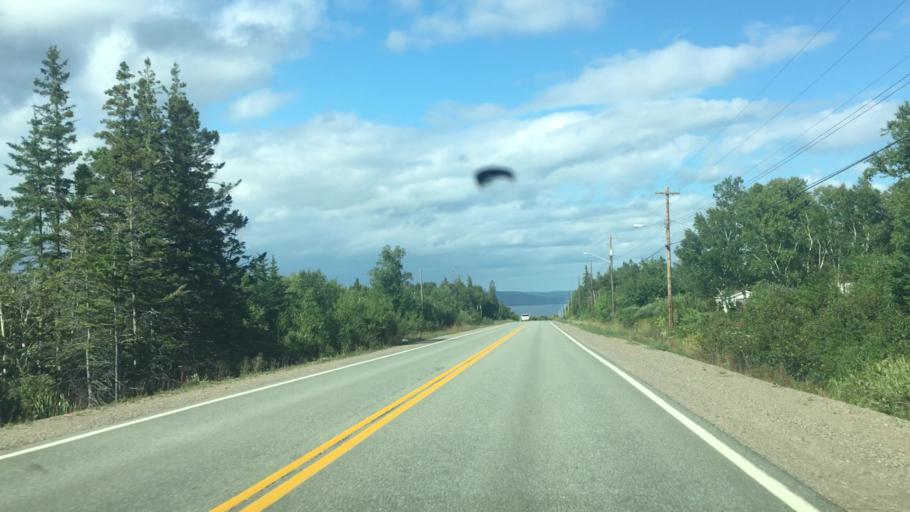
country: CA
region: Nova Scotia
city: Sydney
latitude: 45.8584
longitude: -60.6282
